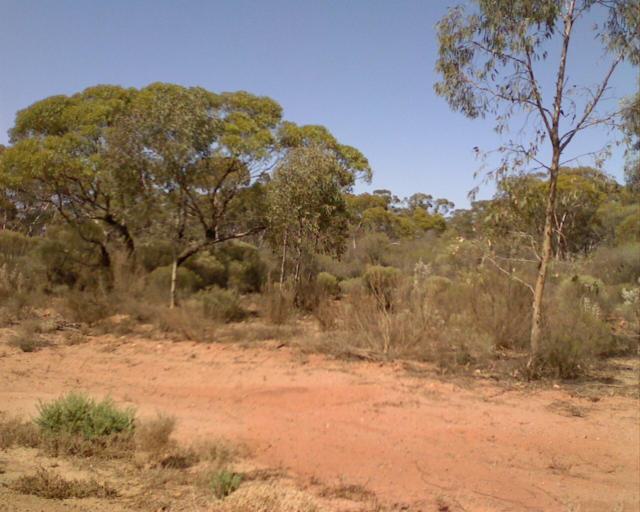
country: AU
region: Western Australia
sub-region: Kalgoorlie/Boulder
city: Boulder
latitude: -30.8279
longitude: 121.3801
